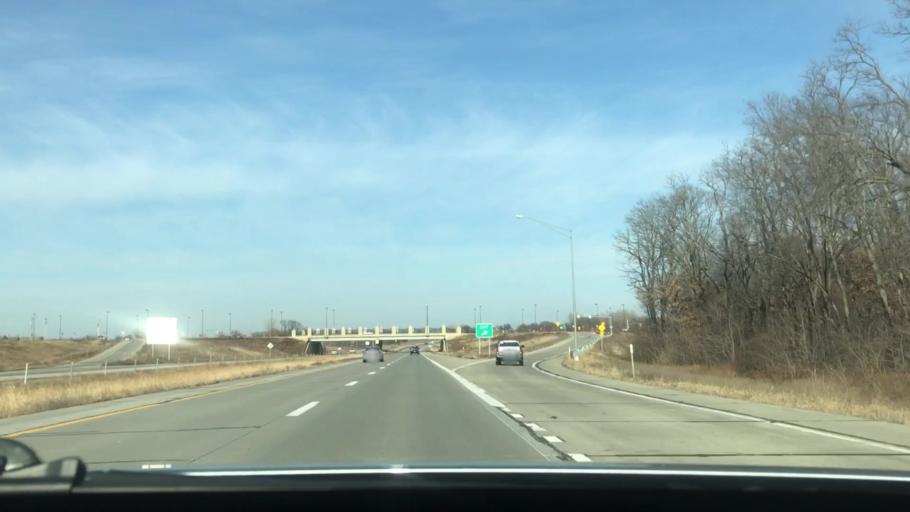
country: US
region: Missouri
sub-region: Clay County
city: Gladstone
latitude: 39.2863
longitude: -94.5850
